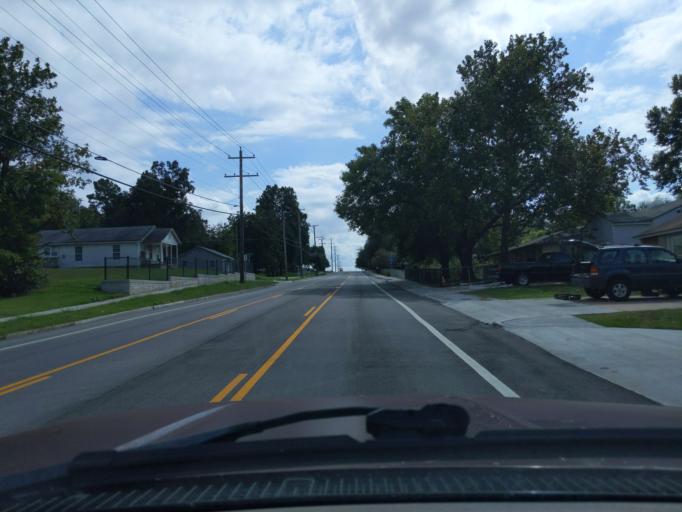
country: US
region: Oklahoma
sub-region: Tulsa County
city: Oakhurst
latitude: 36.0978
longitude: -96.0117
